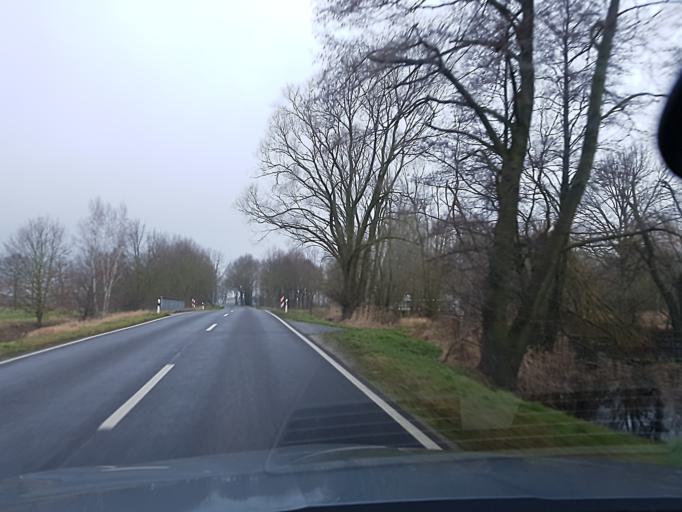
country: DE
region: Brandenburg
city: Doberlug-Kirchhain
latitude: 51.6457
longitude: 13.5578
